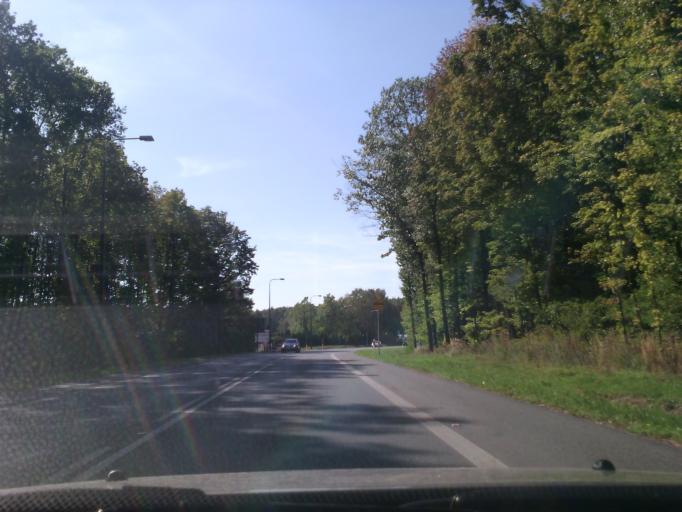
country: PL
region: Silesian Voivodeship
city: Zebrzydowice
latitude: 50.0847
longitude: 18.4957
